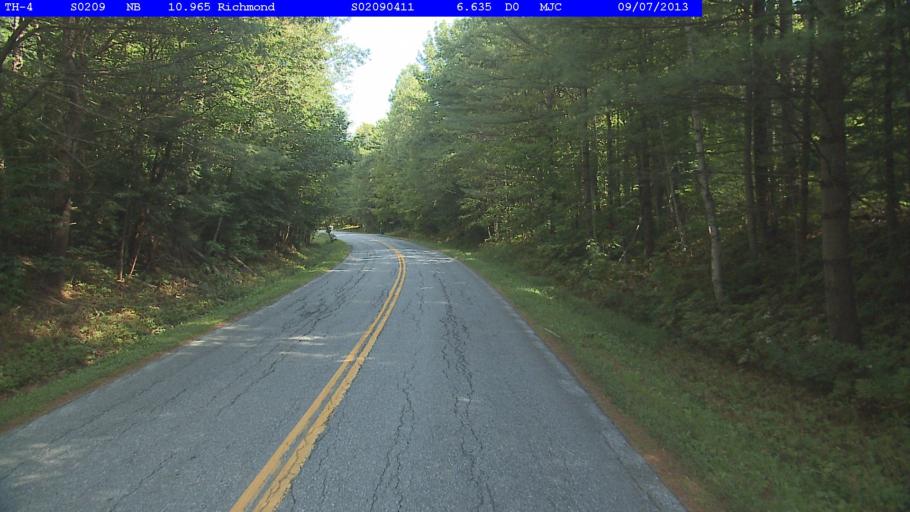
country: US
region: Vermont
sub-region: Chittenden County
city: Jericho
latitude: 44.4202
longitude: -72.9788
